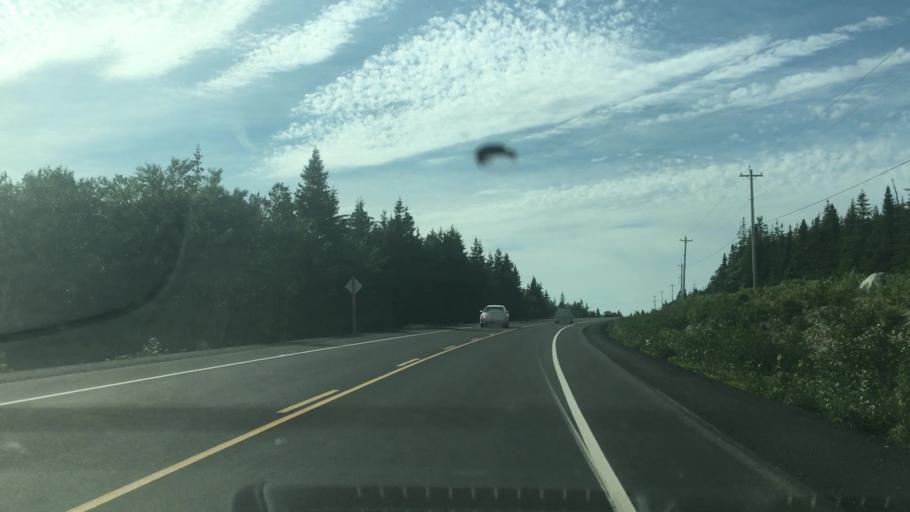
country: CA
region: Nova Scotia
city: Sydney Mines
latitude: 46.8432
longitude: -60.4019
